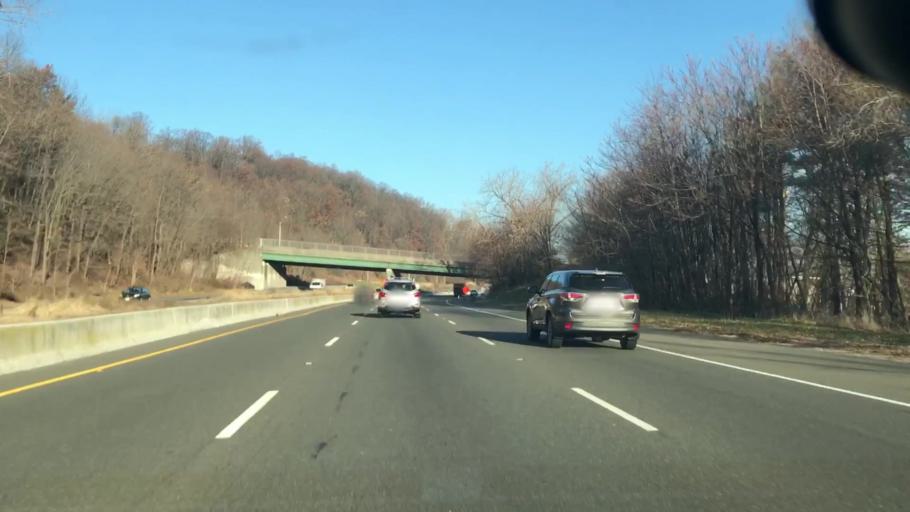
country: US
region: New Jersey
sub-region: Passaic County
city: Paterson
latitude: 40.8975
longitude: -74.1701
